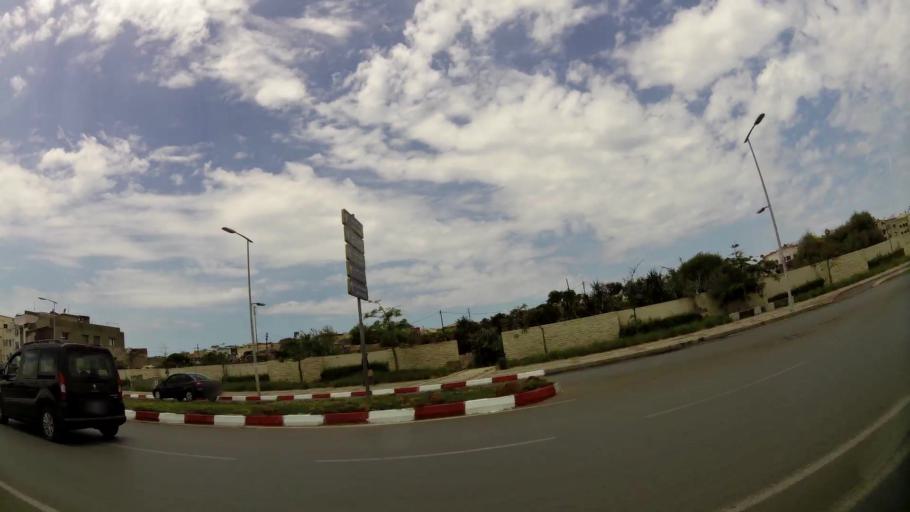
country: MA
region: Rabat-Sale-Zemmour-Zaer
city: Sale
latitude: 34.0460
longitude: -6.8178
